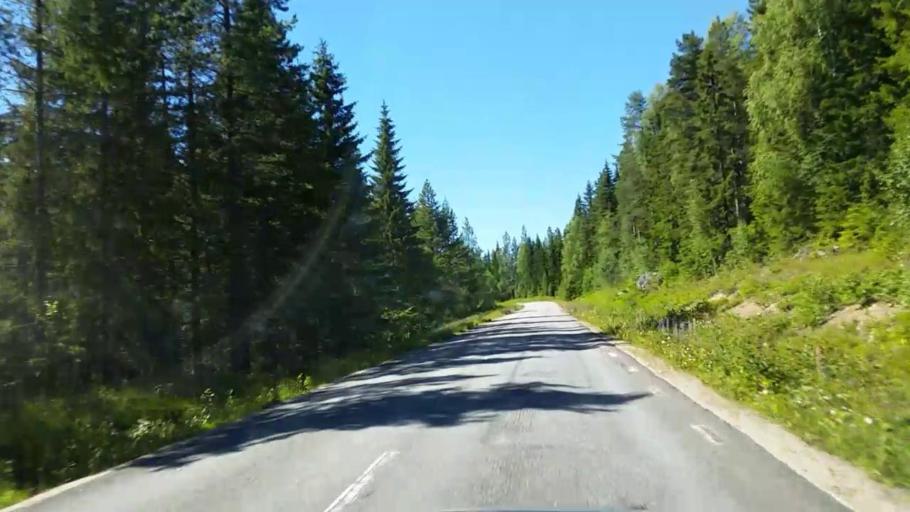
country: SE
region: Gaevleborg
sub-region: Ljusdals Kommun
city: Farila
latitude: 61.6590
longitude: 15.6015
